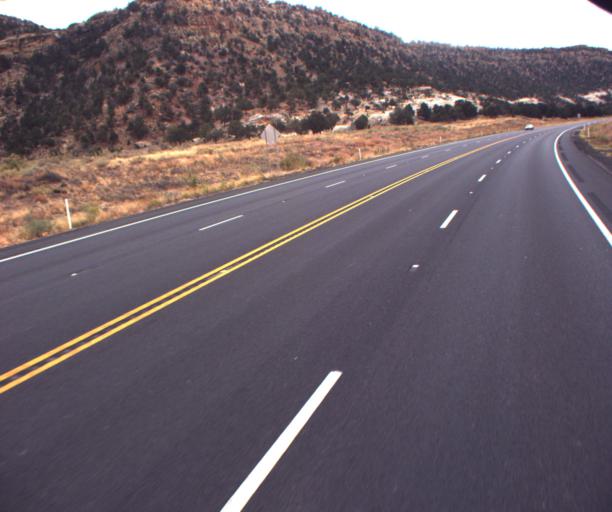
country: US
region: Arizona
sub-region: Navajo County
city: Kayenta
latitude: 36.5805
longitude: -110.4724
